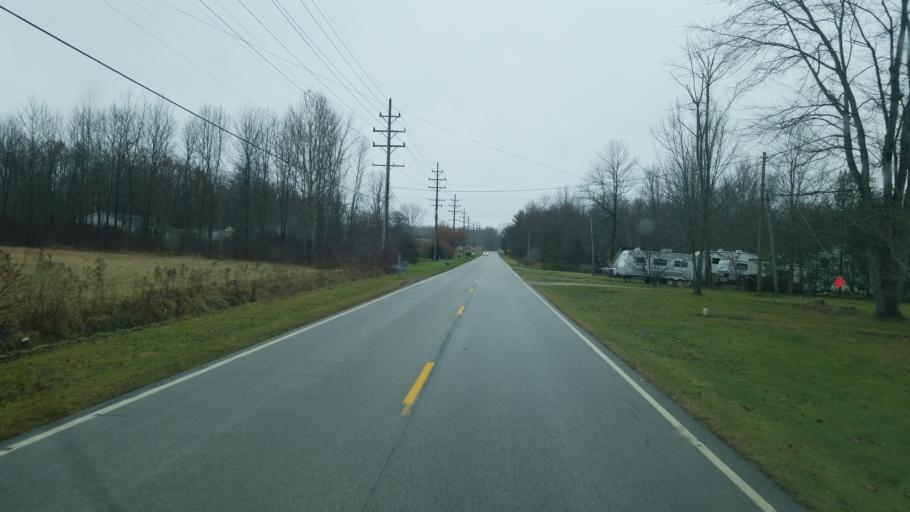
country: US
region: Ohio
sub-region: Ashtabula County
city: Jefferson
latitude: 41.7651
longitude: -80.8099
